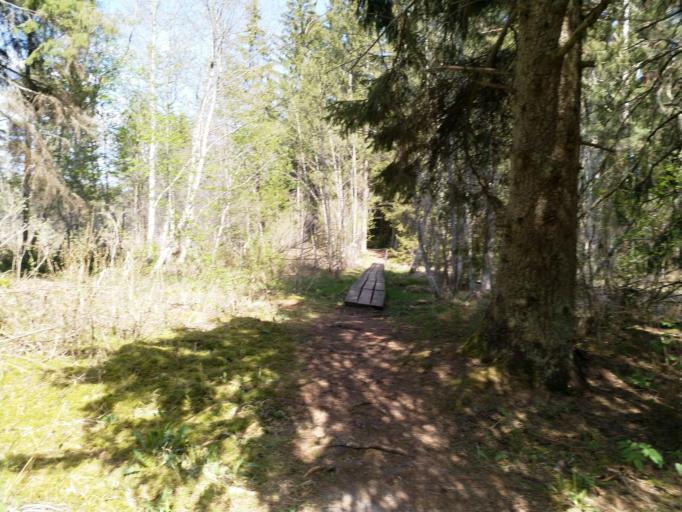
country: LV
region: Kandava
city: Kandava
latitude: 57.0213
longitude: 22.7742
